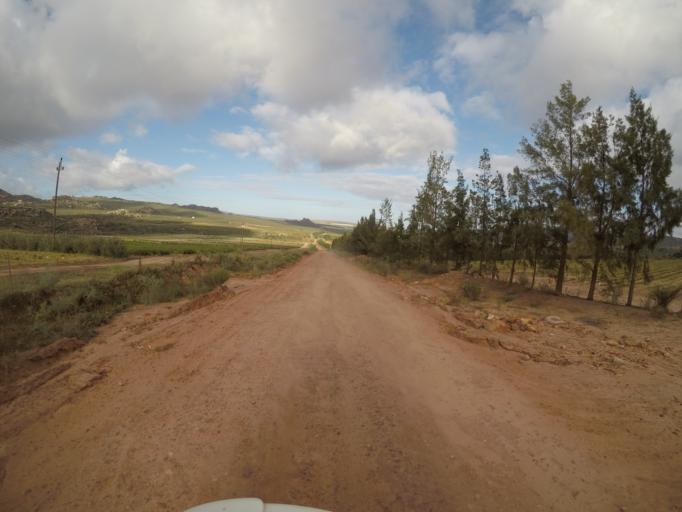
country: ZA
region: Western Cape
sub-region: West Coast District Municipality
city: Clanwilliam
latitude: -32.3445
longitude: 18.7544
